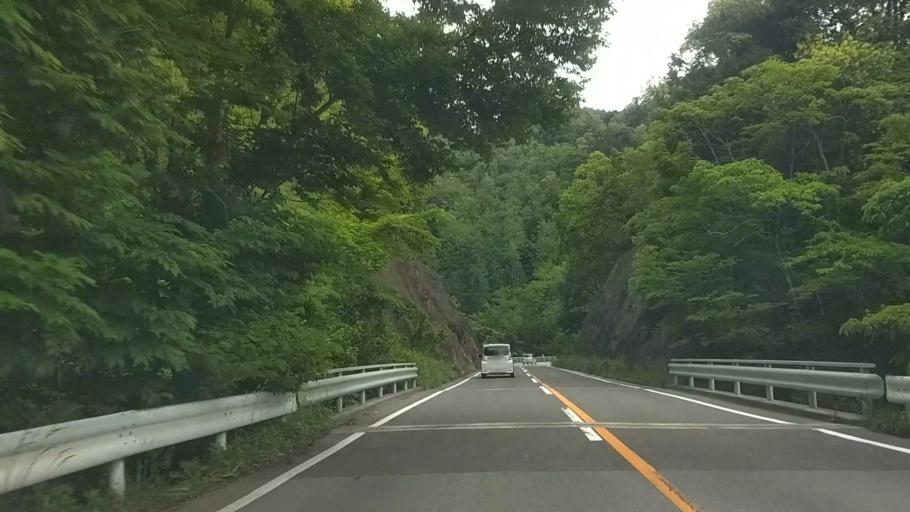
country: JP
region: Yamanashi
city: Isawa
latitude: 35.5651
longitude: 138.5938
